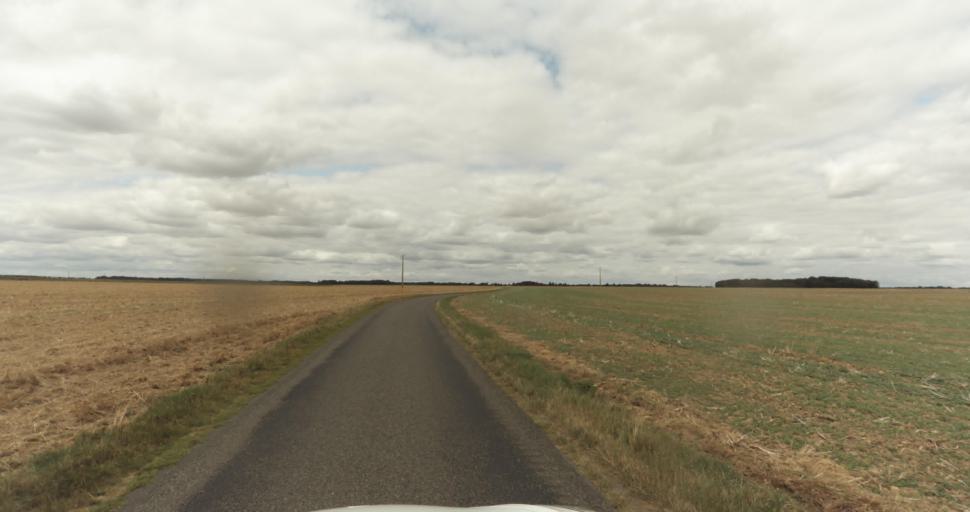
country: FR
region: Haute-Normandie
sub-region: Departement de l'Eure
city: Saint-Germain-sur-Avre
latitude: 48.8028
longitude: 1.2584
